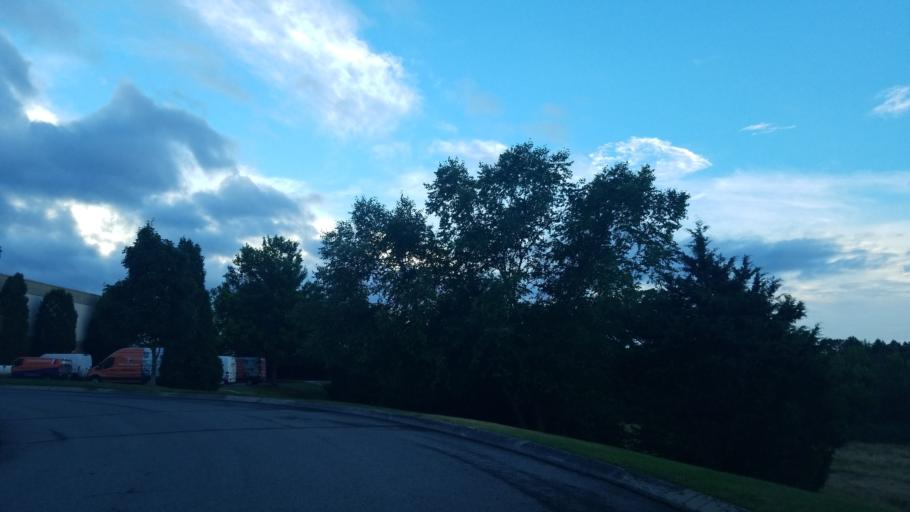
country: US
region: Tennessee
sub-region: Rutherford County
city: La Vergne
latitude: 36.1052
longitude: -86.6387
